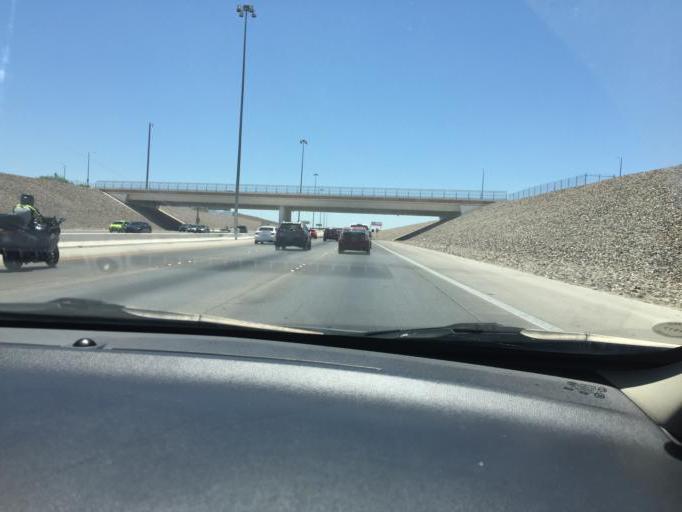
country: US
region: Nevada
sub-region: Clark County
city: Whitney
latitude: 36.0367
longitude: -115.1338
